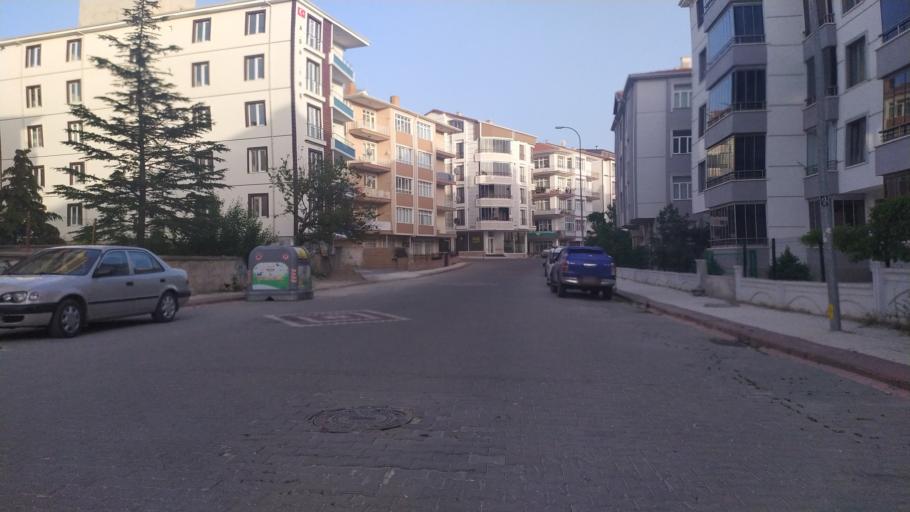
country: TR
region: Kirsehir
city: Kirsehir
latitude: 39.1514
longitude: 34.1580
